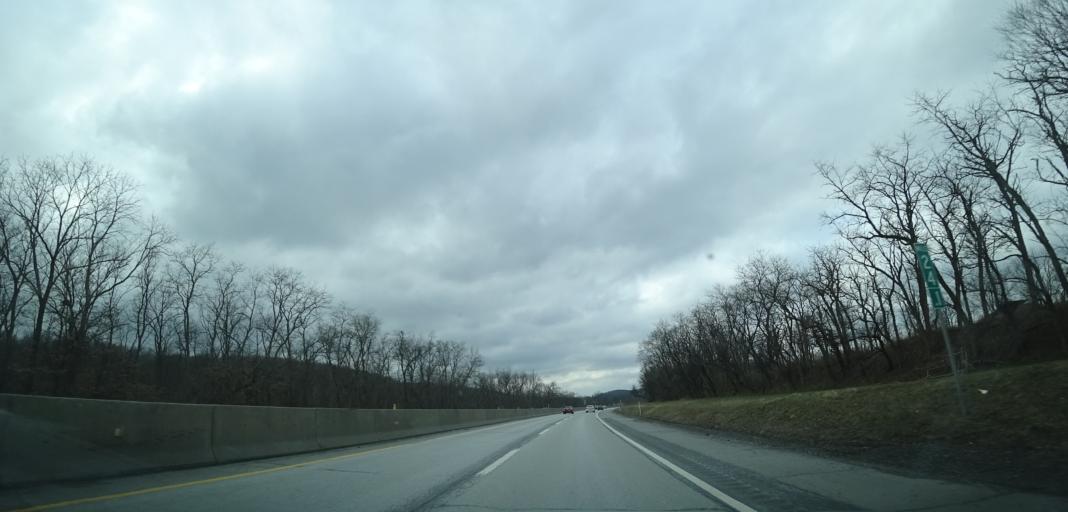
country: US
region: Pennsylvania
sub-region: Butler County
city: Fernway
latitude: 40.7251
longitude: -80.1568
